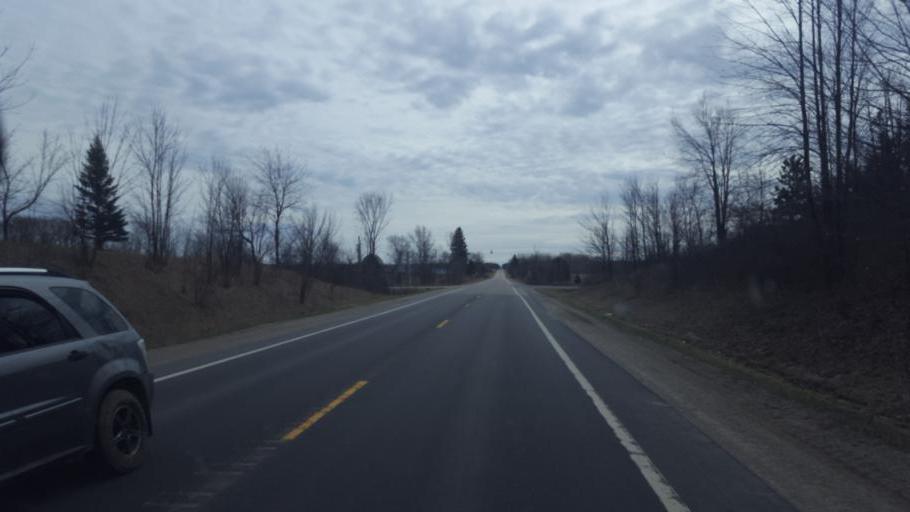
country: US
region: Michigan
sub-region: Isabella County
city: Lake Isabella
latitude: 43.7127
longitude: -85.1467
